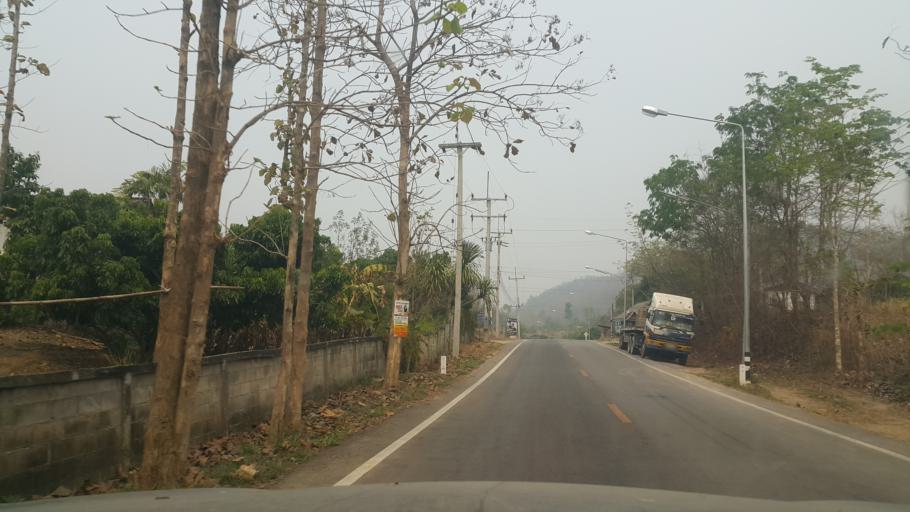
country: TH
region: Lamphun
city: Mae Tha
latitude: 18.4686
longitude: 99.1798
